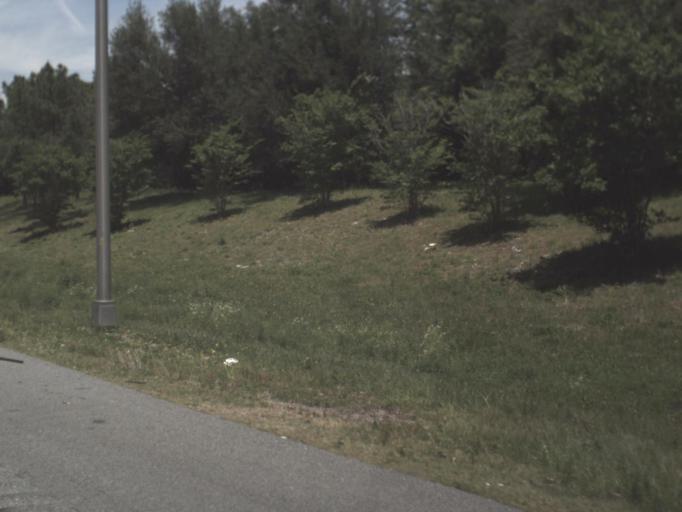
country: US
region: Florida
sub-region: Duval County
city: Jacksonville
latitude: 30.3345
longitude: -81.5351
